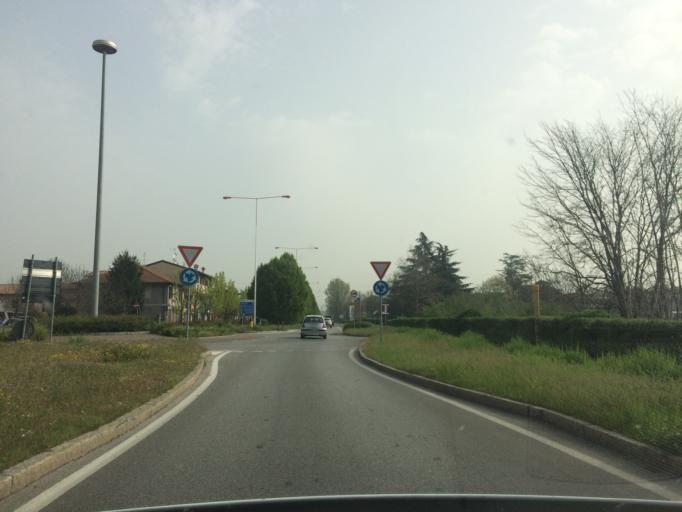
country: IT
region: Lombardy
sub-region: Provincia di Brescia
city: Flero
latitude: 45.5048
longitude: 10.1743
